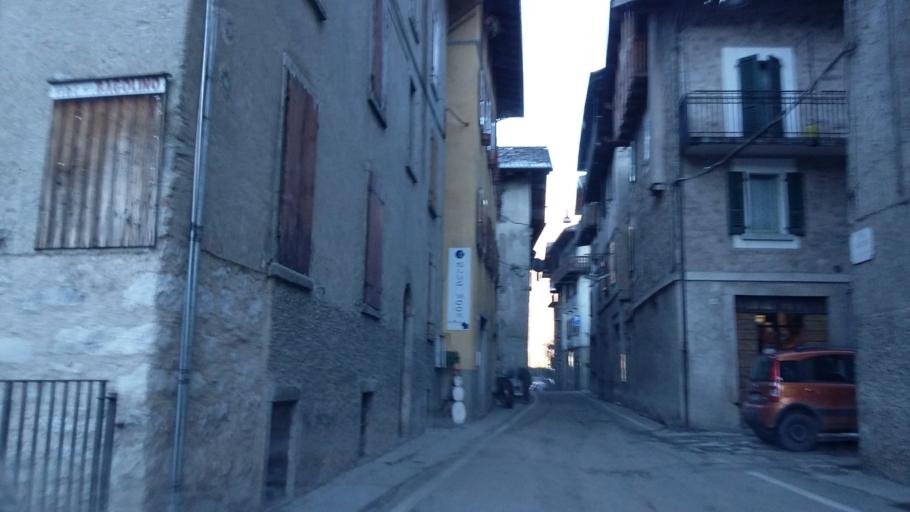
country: IT
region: Lombardy
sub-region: Provincia di Brescia
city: Bagolino
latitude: 45.8234
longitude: 10.4624
